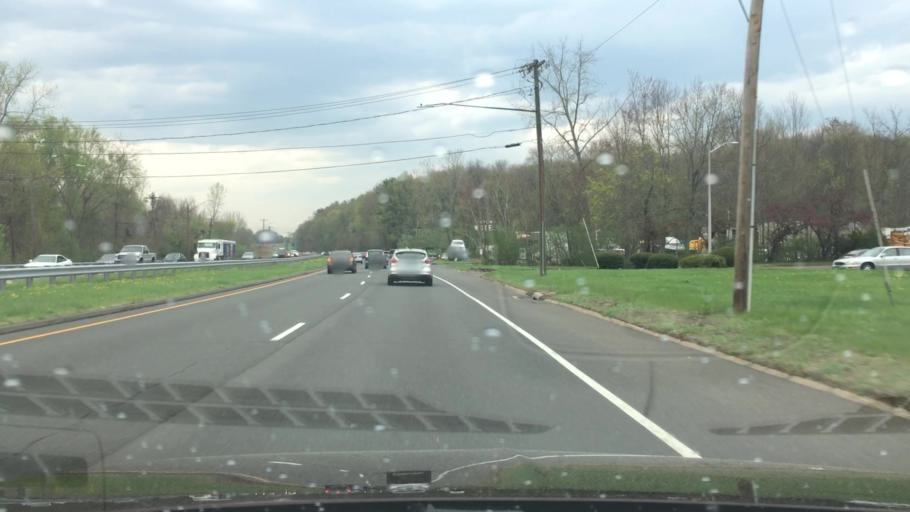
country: US
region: Connecticut
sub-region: Hartford County
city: Kensington
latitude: 41.6160
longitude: -72.7434
